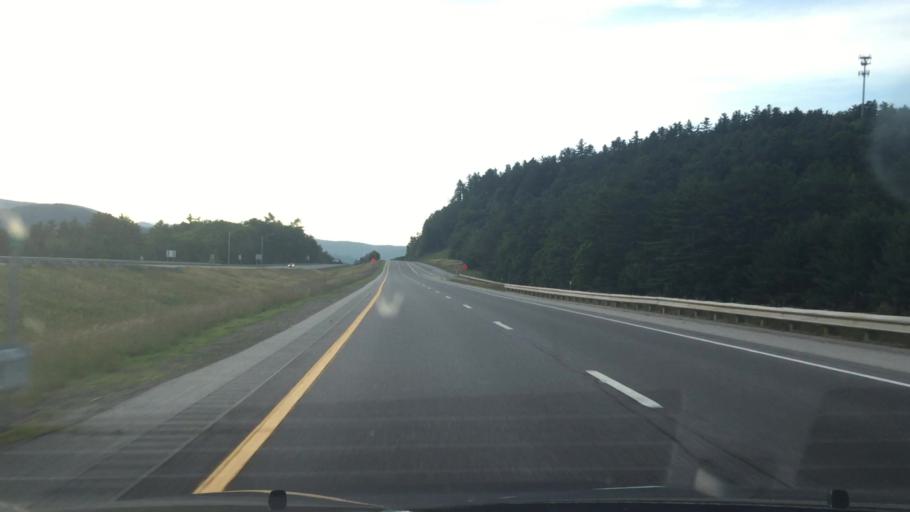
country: US
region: New Hampshire
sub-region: Grafton County
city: Thornton
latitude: 43.8515
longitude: -71.6463
